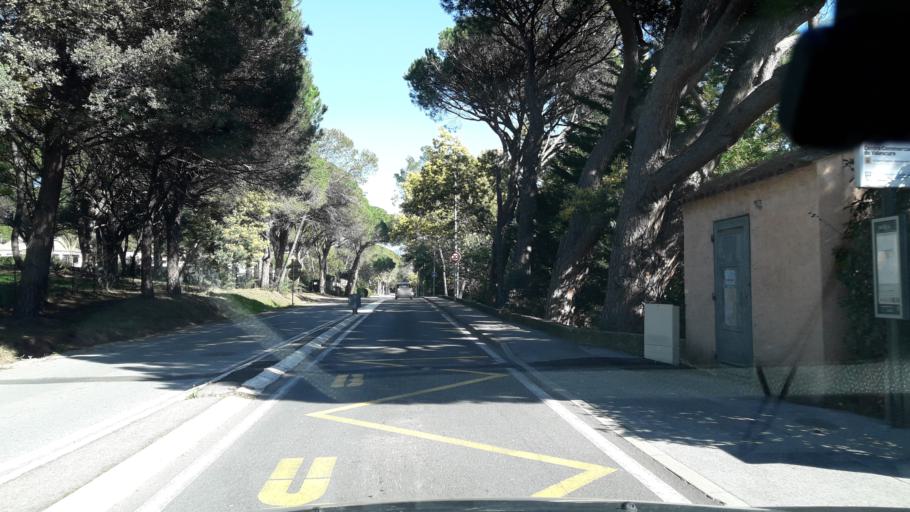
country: FR
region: Provence-Alpes-Cote d'Azur
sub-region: Departement du Var
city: Saint-Raphael
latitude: 43.4534
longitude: 6.7837
